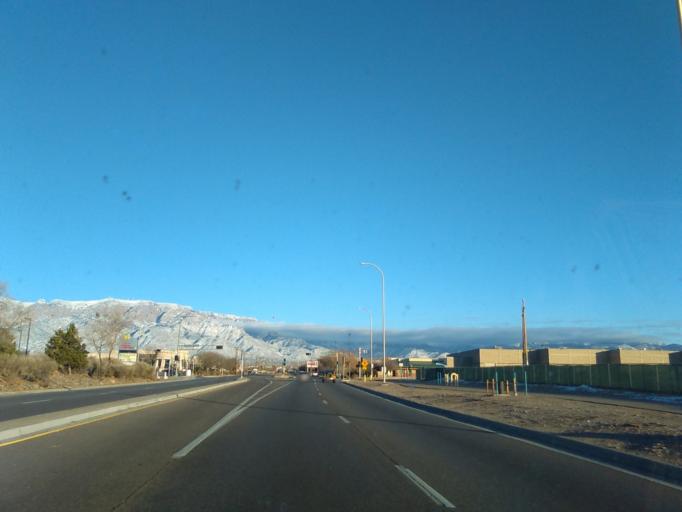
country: US
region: New Mexico
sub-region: Bernalillo County
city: North Valley
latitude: 35.1845
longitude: -106.6001
